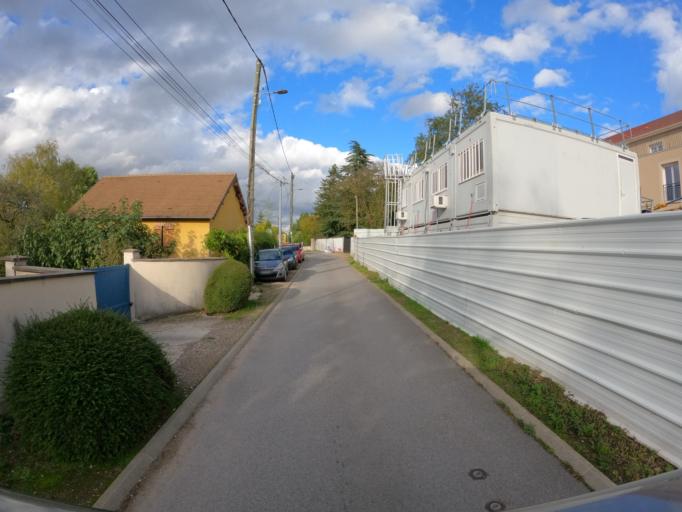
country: FR
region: Ile-de-France
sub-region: Departement de Seine-et-Marne
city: Chalifert
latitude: 48.8885
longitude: 2.7712
